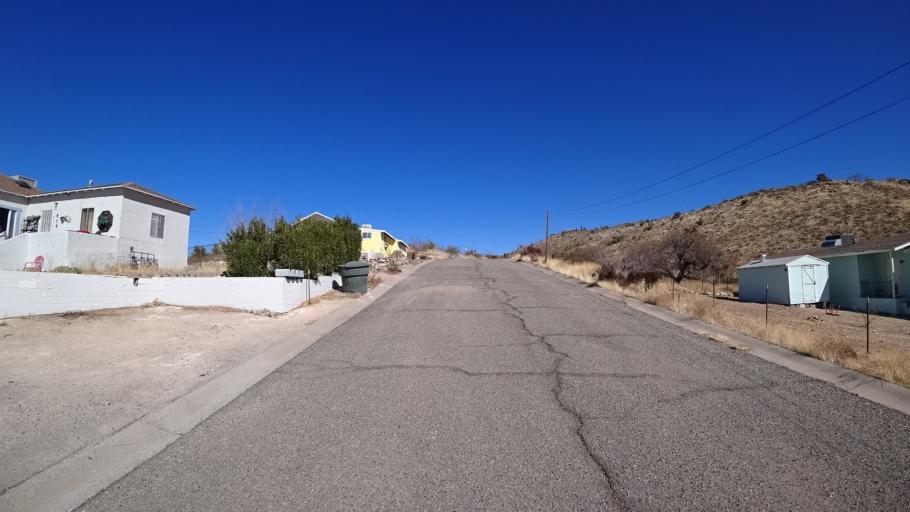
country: US
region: Arizona
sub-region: Mohave County
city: Kingman
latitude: 35.1954
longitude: -114.0572
